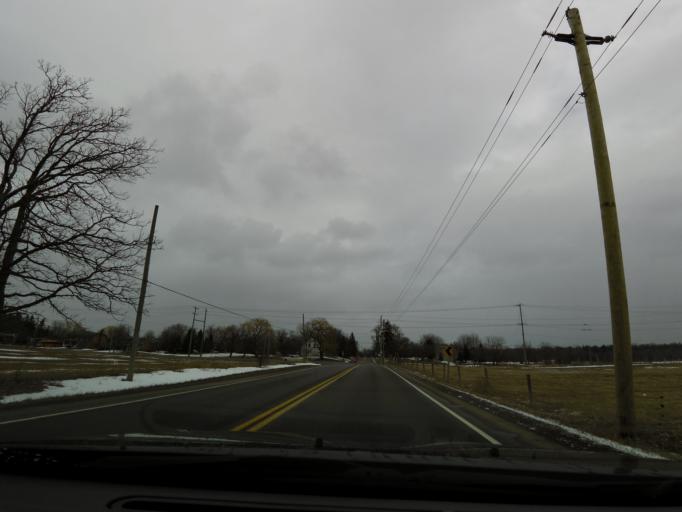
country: CA
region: Ontario
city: Ancaster
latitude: 43.2882
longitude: -79.9472
